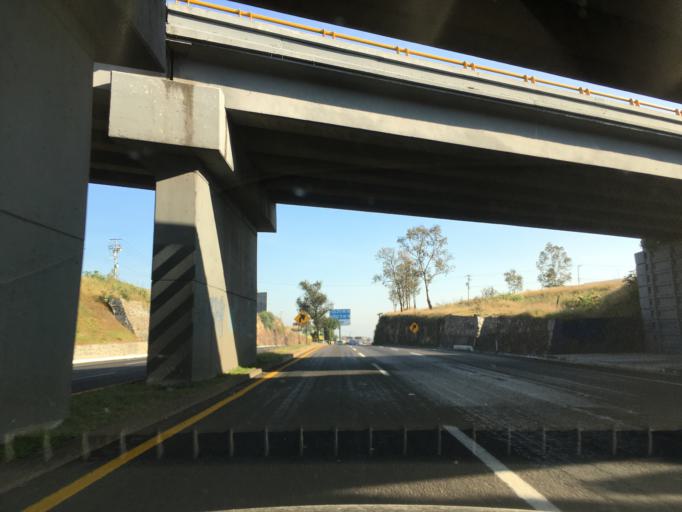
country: MX
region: Michoacan
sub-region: Tarimbaro
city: San Bernabe de las Canteras
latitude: 19.7583
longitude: -101.1678
